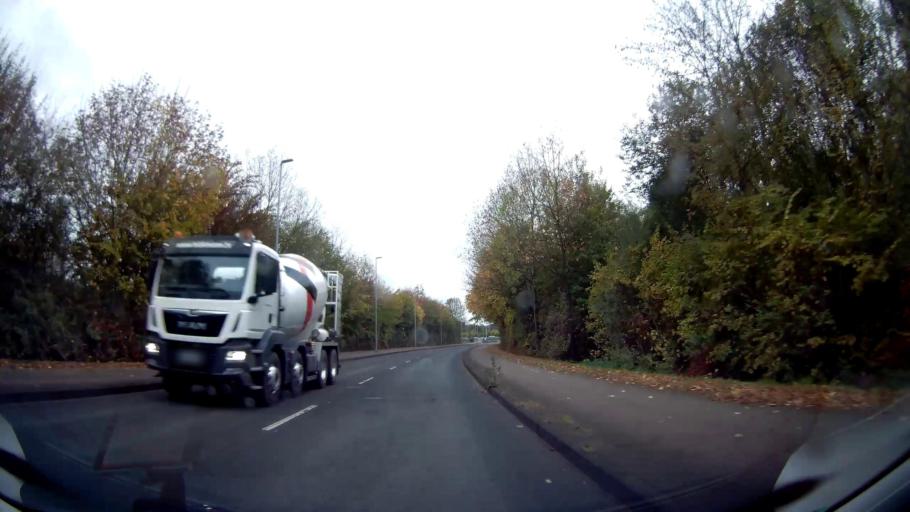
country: DE
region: North Rhine-Westphalia
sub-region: Regierungsbezirk Munster
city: Gladbeck
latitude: 51.5494
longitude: 6.9646
